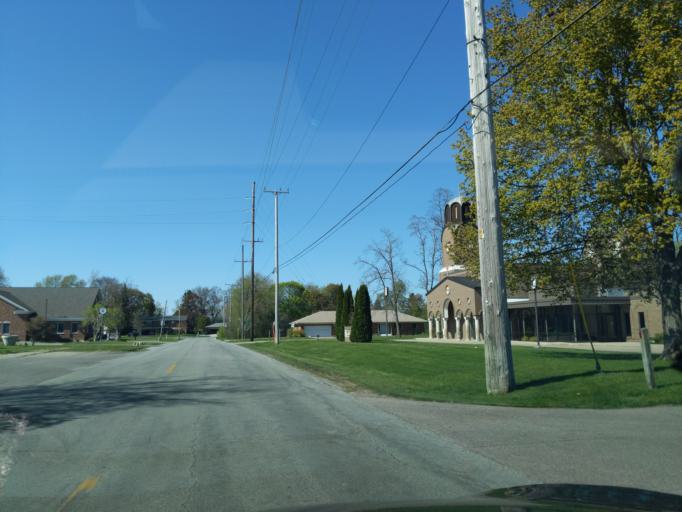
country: US
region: Michigan
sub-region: Kent County
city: East Grand Rapids
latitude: 42.9683
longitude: -85.6177
